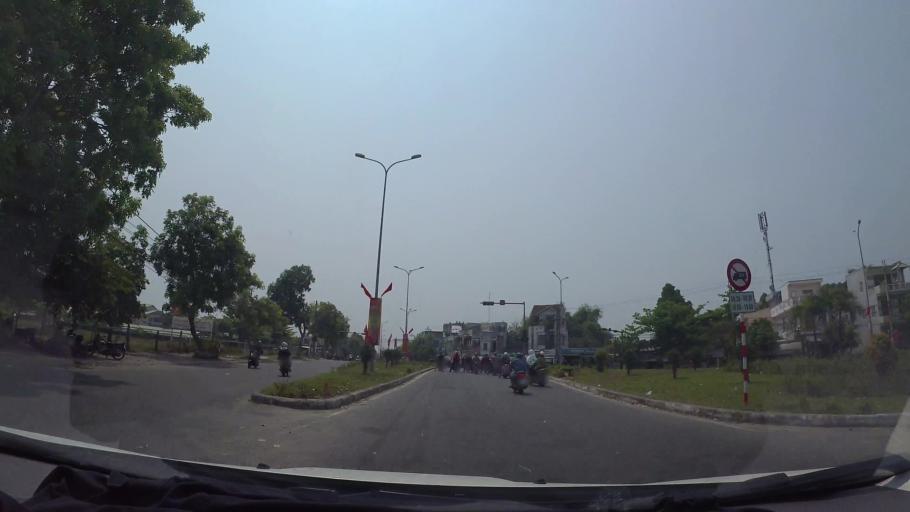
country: VN
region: Da Nang
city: Cam Le
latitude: 15.9809
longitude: 108.2081
